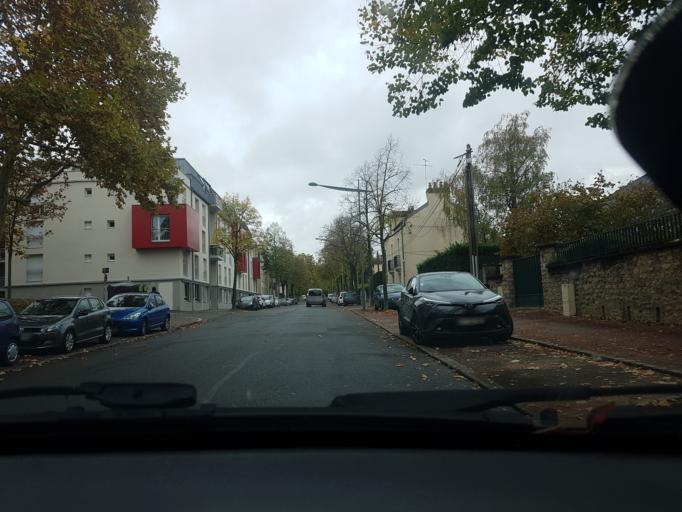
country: FR
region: Bourgogne
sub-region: Departement de la Cote-d'Or
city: Saint-Apollinaire
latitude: 47.3211
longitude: 5.0575
